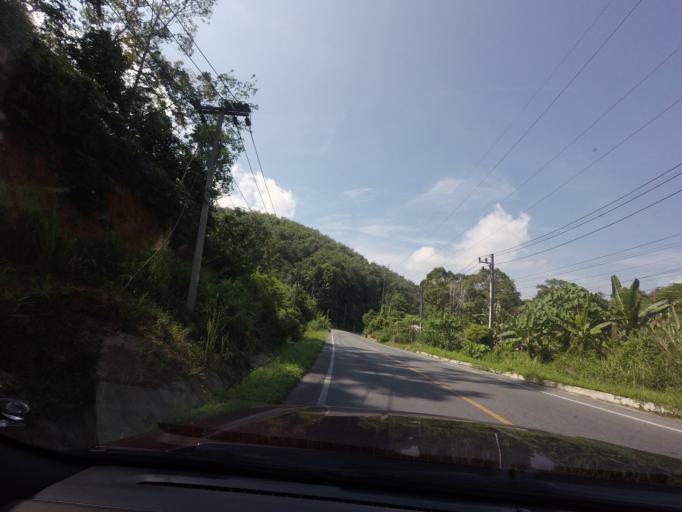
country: TH
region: Yala
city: Betong
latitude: 5.8896
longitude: 101.1456
